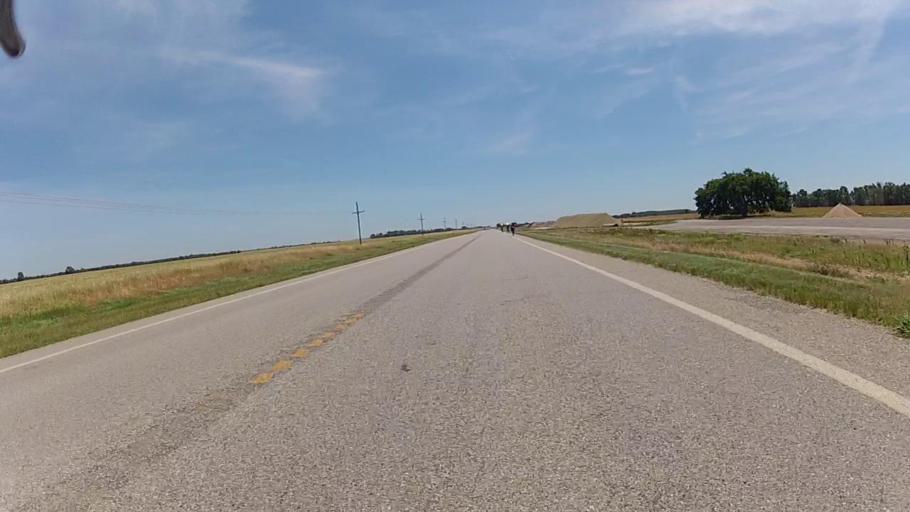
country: US
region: Kansas
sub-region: Barber County
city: Medicine Lodge
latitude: 37.2543
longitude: -98.5097
